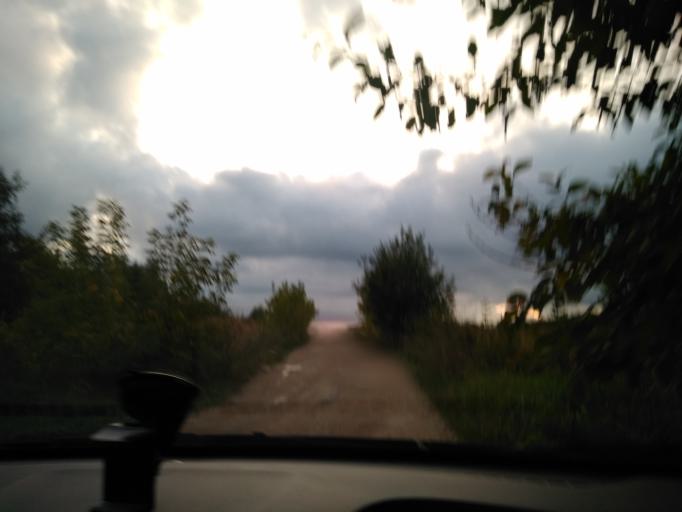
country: RU
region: Moskovskaya
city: Ramenskoye
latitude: 55.5026
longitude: 38.1781
